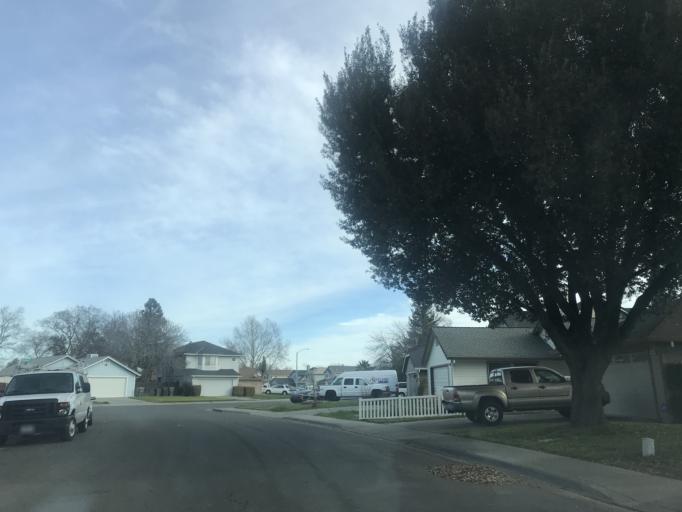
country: US
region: California
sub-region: Yolo County
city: Woodland
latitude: 38.6643
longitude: -121.7536
